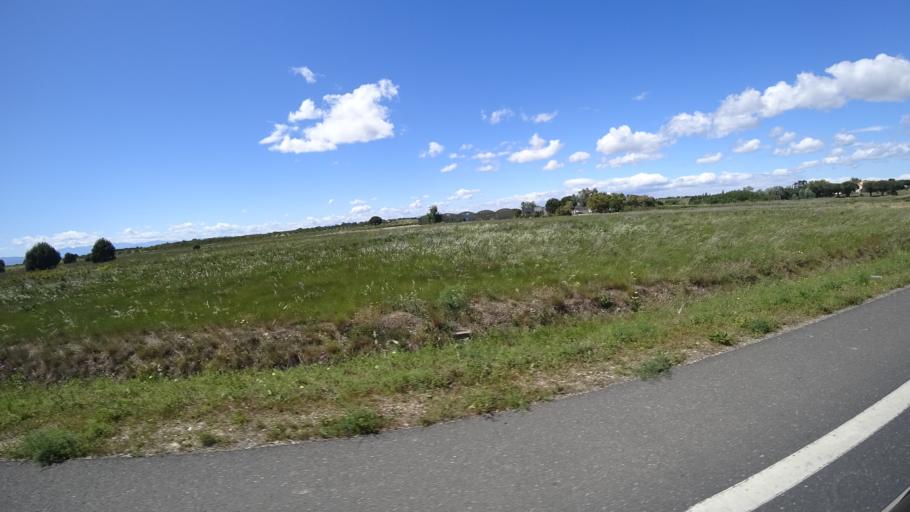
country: FR
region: Languedoc-Roussillon
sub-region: Departement des Pyrenees-Orientales
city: Saint-Nazaire
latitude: 42.6785
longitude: 2.9924
